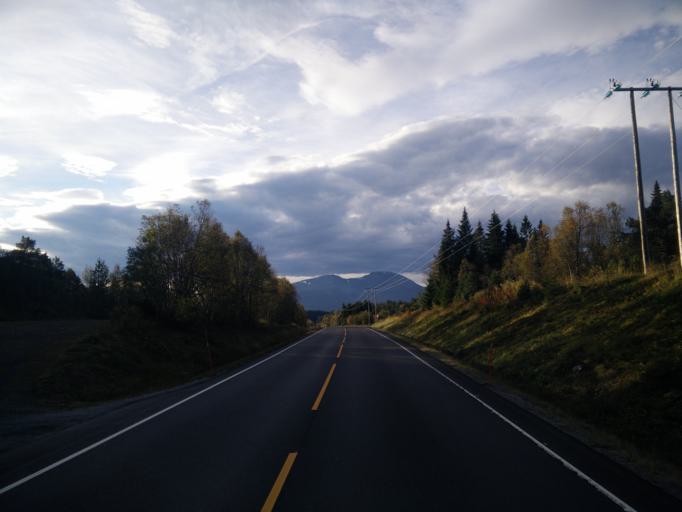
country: NO
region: More og Romsdal
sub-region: Gjemnes
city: Batnfjordsora
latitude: 62.8368
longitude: 7.6007
